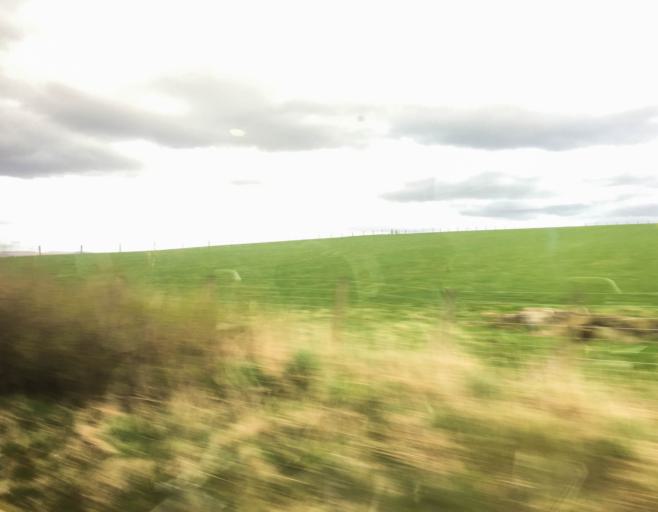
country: GB
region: Scotland
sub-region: South Lanarkshire
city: Carnwath
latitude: 55.6532
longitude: -3.6333
